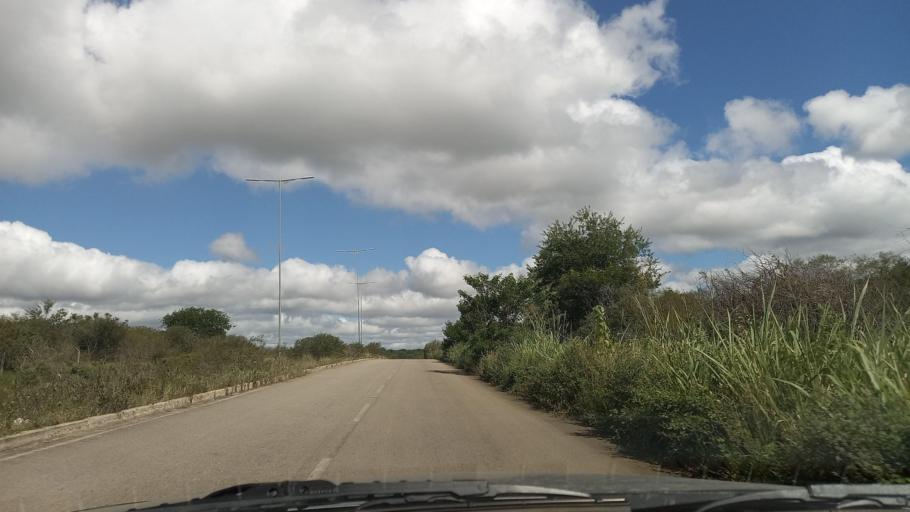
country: BR
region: Pernambuco
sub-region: Caruaru
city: Caruaru
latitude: -8.2236
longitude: -35.9852
